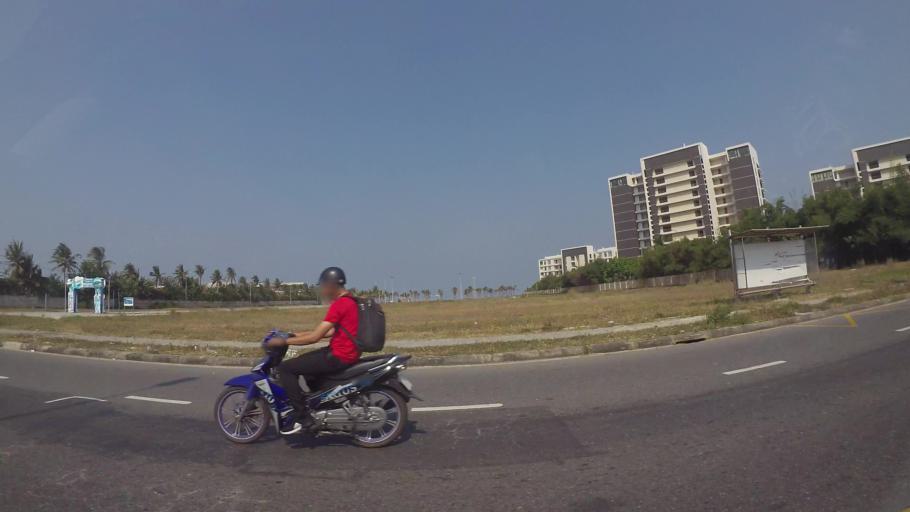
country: VN
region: Da Nang
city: Ngu Hanh Son
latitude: 16.0150
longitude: 108.2610
